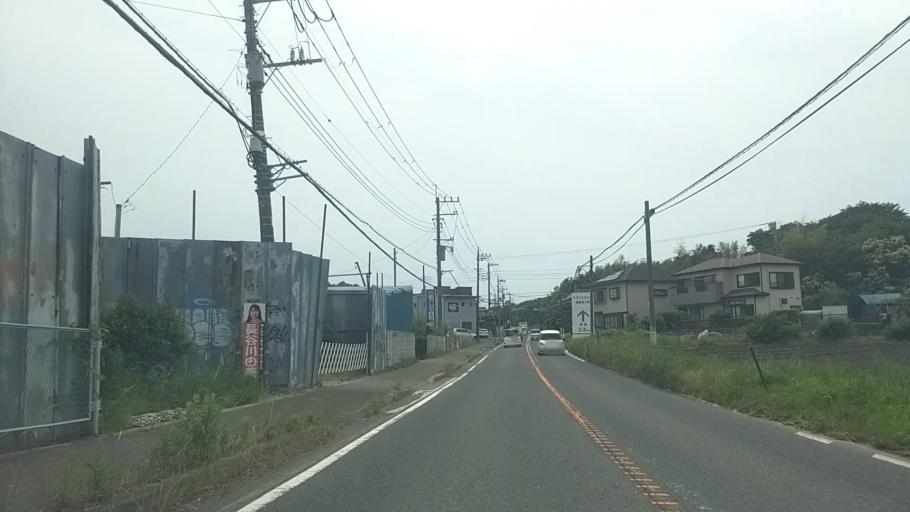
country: JP
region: Kanagawa
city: Chigasaki
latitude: 35.3623
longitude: 139.4220
